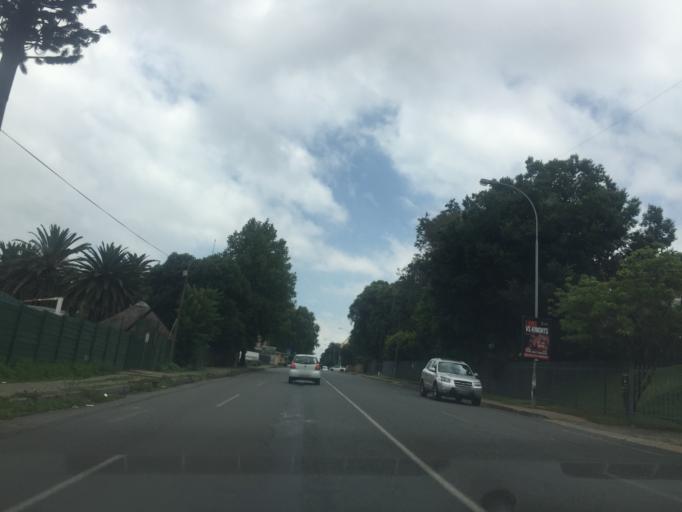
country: ZA
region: Gauteng
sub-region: City of Johannesburg Metropolitan Municipality
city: Johannesburg
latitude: -26.1327
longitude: 28.0515
